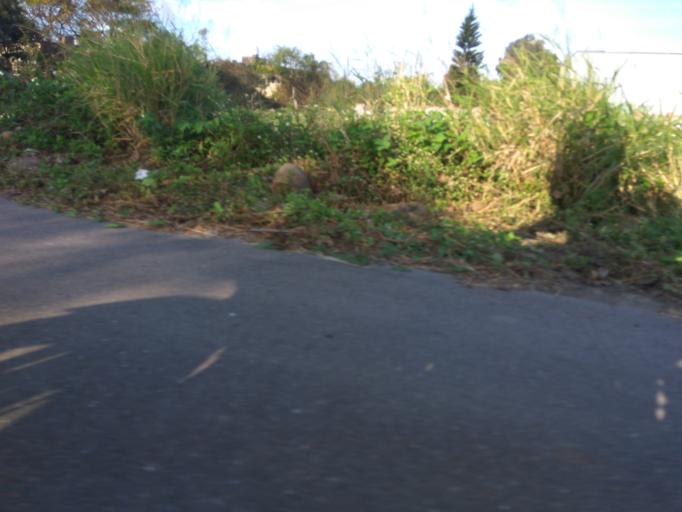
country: TW
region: Taiwan
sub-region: Hsinchu
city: Zhubei
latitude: 24.9811
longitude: 121.0546
